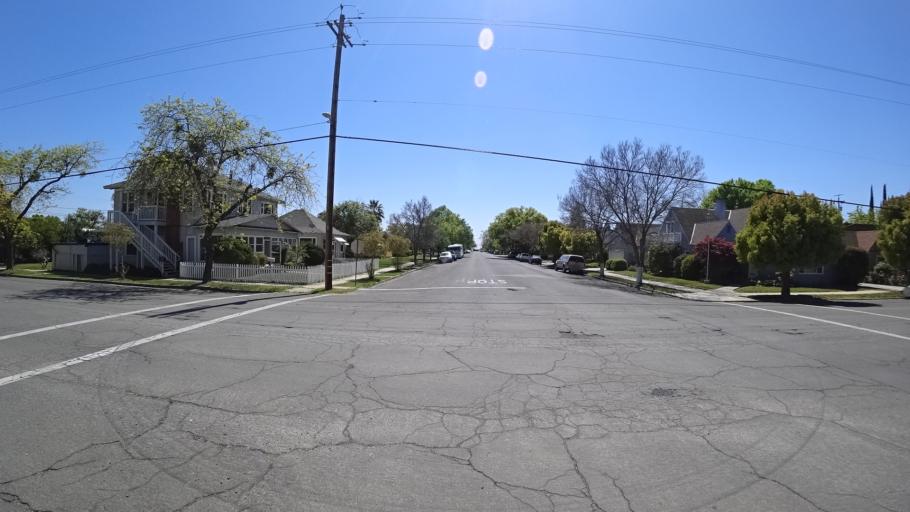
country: US
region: California
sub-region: Glenn County
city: Willows
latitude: 39.5179
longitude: -122.1982
